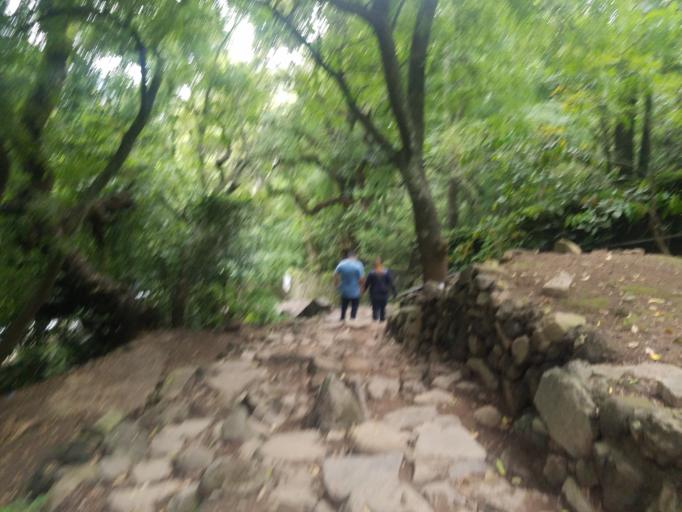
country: MX
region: Morelos
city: Tepoztlan
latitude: 18.9967
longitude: -99.0996
